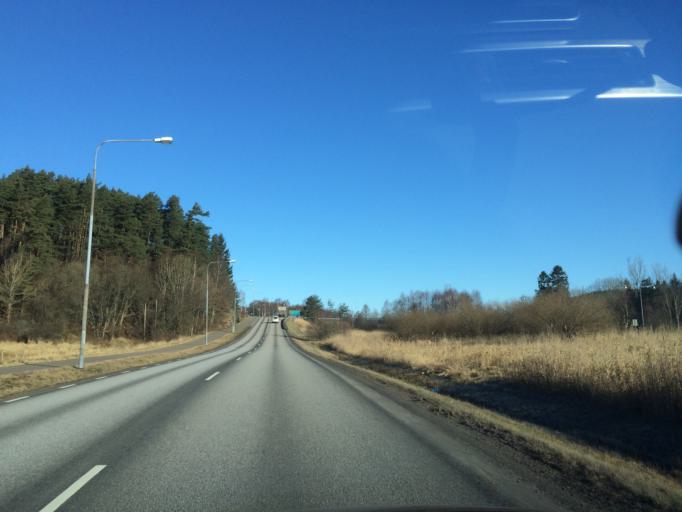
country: SE
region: Vaestra Goetaland
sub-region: Molndal
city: Kallered
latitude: 57.6206
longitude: 12.0358
